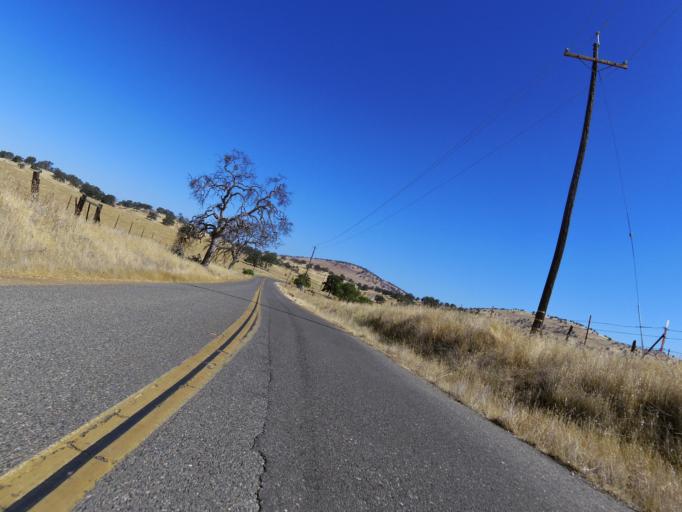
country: US
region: California
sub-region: Merced County
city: Planada
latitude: 37.6039
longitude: -120.3071
